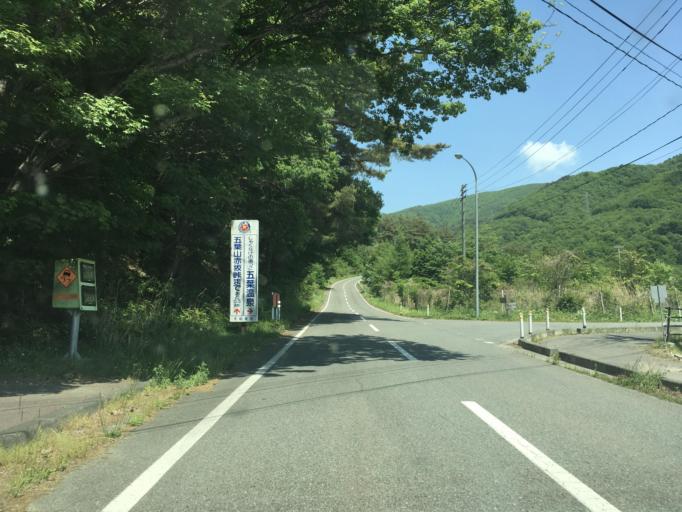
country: JP
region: Iwate
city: Ofunato
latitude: 39.1634
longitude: 141.7117
